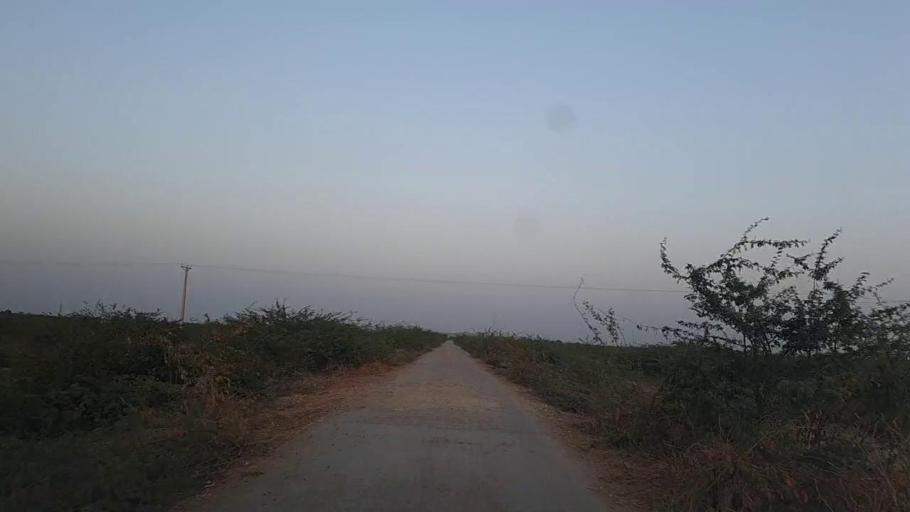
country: PK
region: Sindh
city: Naukot
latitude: 24.7200
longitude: 69.2948
